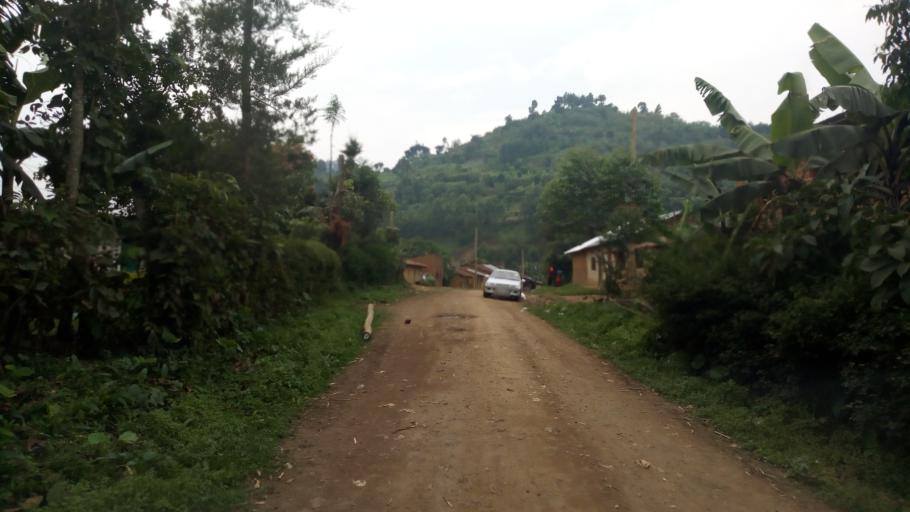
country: UG
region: Western Region
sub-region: Kisoro District
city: Kisoro
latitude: -1.2605
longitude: 29.6288
